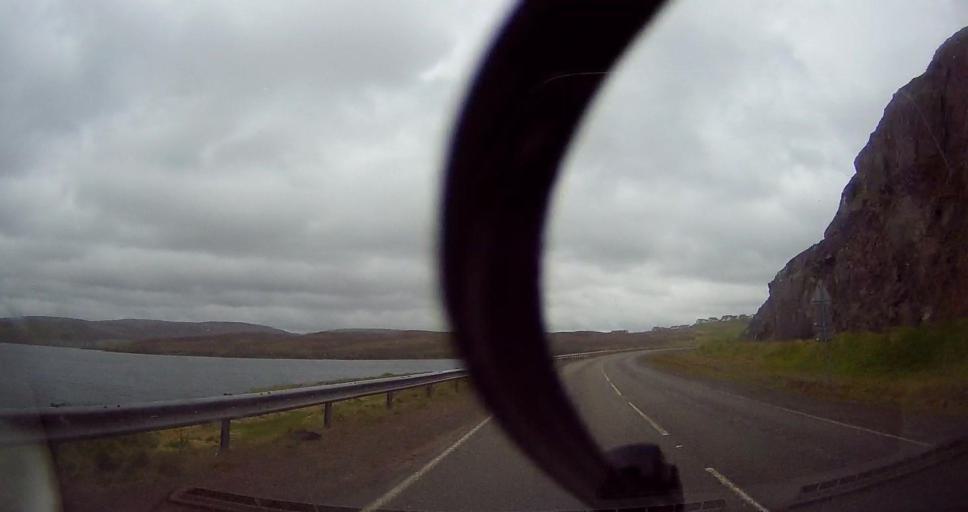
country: GB
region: Scotland
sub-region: Shetland Islands
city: Lerwick
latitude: 60.3973
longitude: -1.3836
